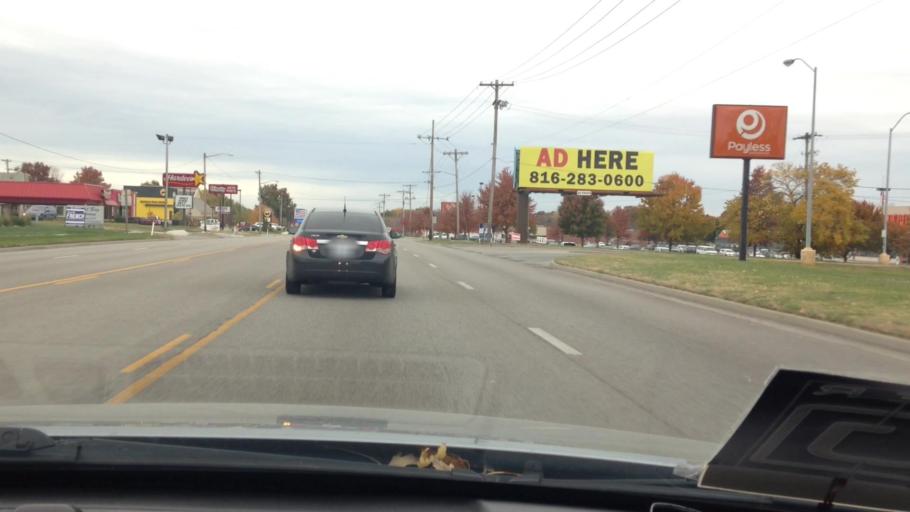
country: US
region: Kansas
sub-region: Leavenworth County
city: Lansing
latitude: 39.2714
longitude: -94.8999
